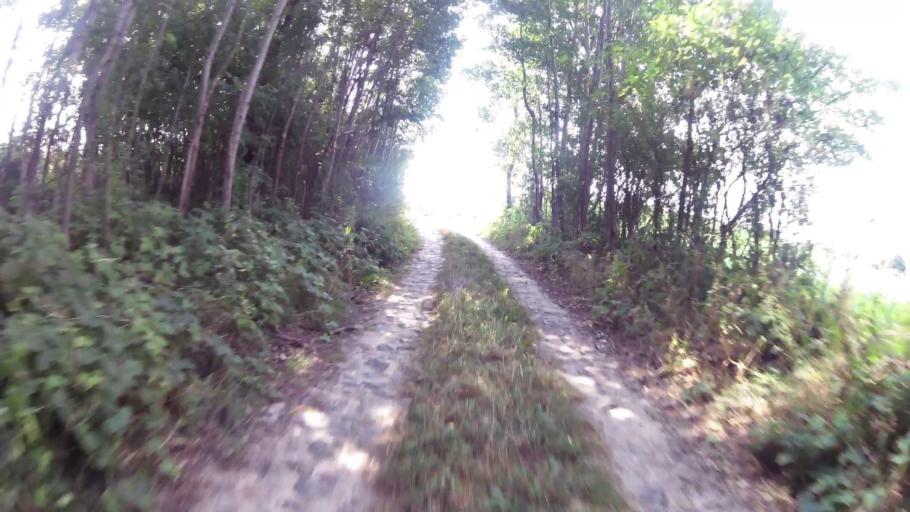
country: PL
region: West Pomeranian Voivodeship
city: Trzcinsko Zdroj
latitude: 52.8993
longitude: 14.5210
